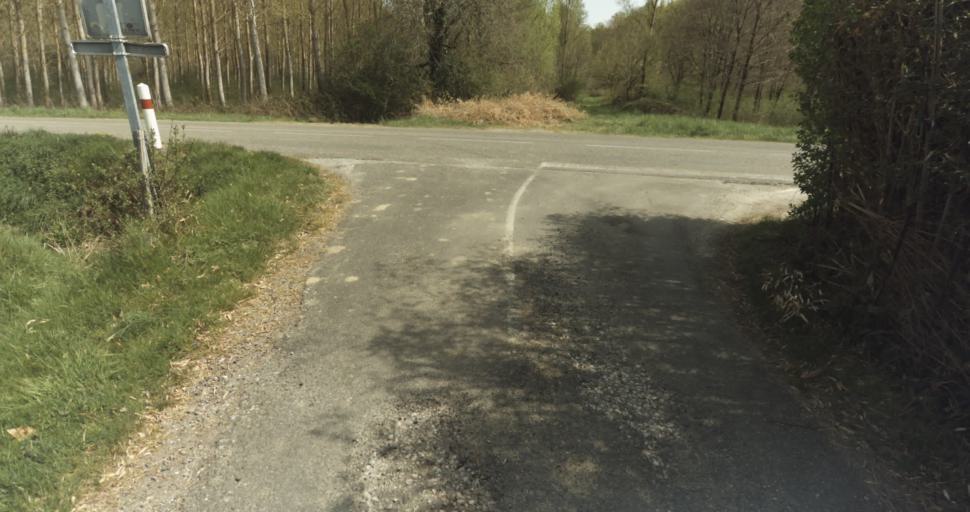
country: FR
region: Midi-Pyrenees
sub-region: Departement du Tarn-et-Garonne
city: Moissac
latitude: 44.1491
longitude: 1.1069
